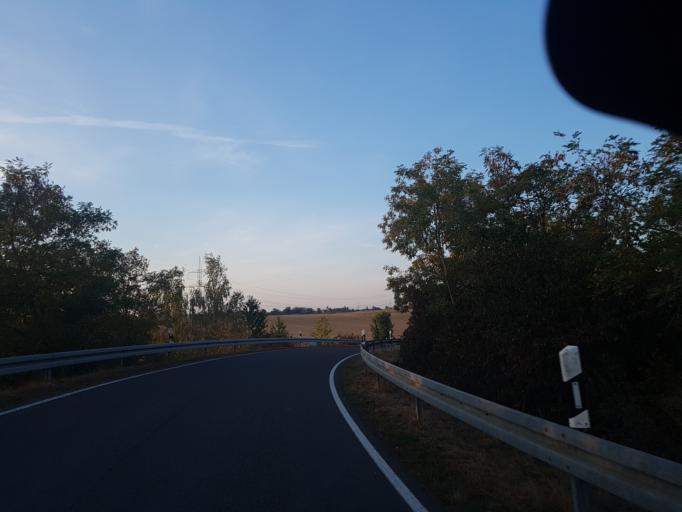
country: DE
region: Saxony
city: Stauchitz
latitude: 51.3038
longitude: 13.1878
